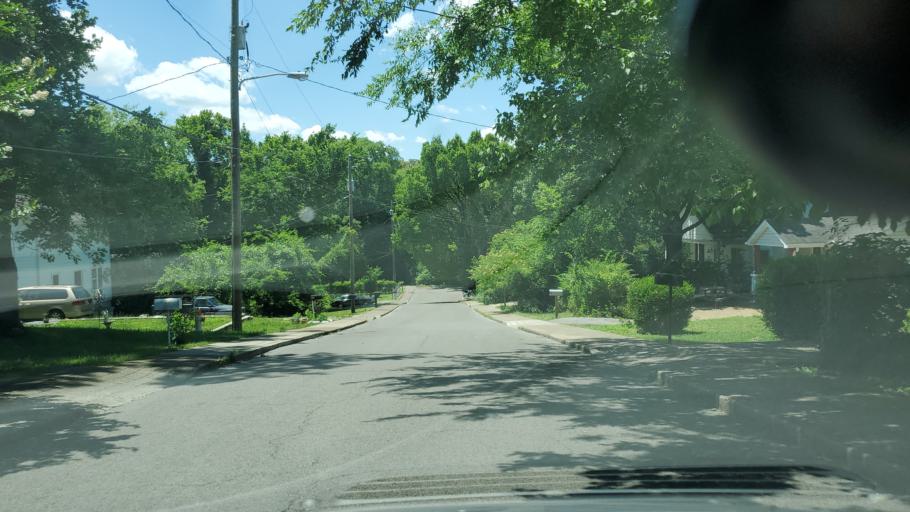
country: US
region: Tennessee
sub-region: Davidson County
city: Nashville
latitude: 36.1916
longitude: -86.7549
